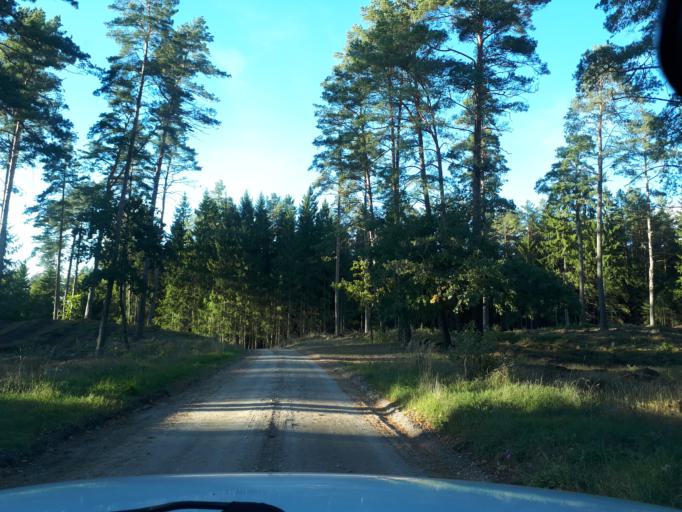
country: LT
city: Kulautuva
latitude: 54.9313
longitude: 23.5859
